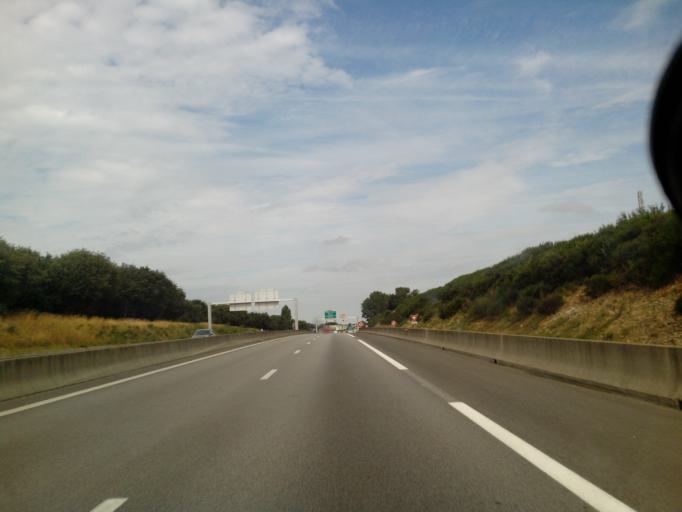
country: FR
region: Brittany
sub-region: Departement du Morbihan
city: Theix
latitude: 47.6421
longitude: -2.6883
